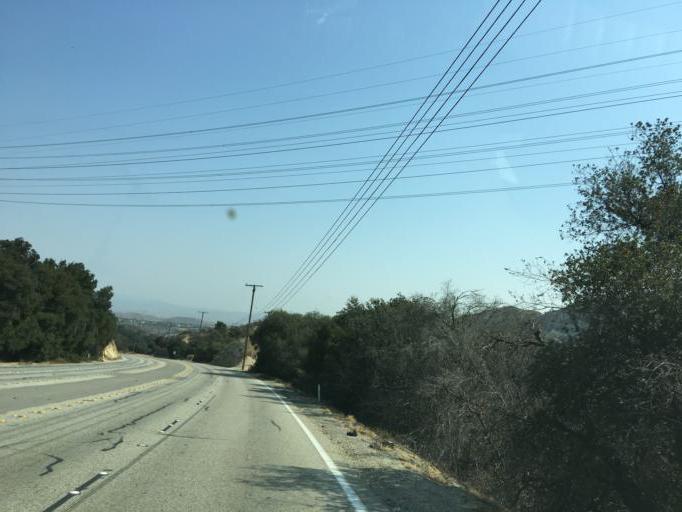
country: US
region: California
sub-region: Los Angeles County
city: Santa Clarita
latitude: 34.3497
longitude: -118.5081
